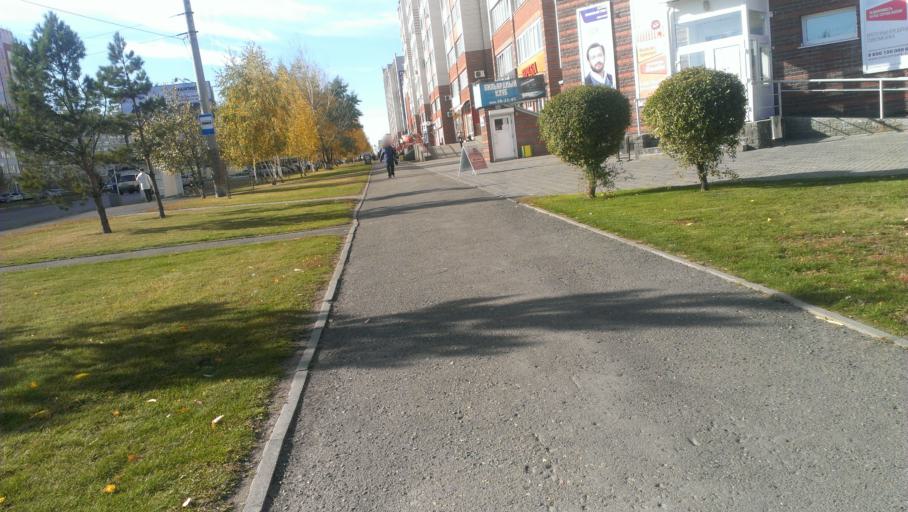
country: RU
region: Altai Krai
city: Novosilikatnyy
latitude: 53.3341
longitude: 83.6926
